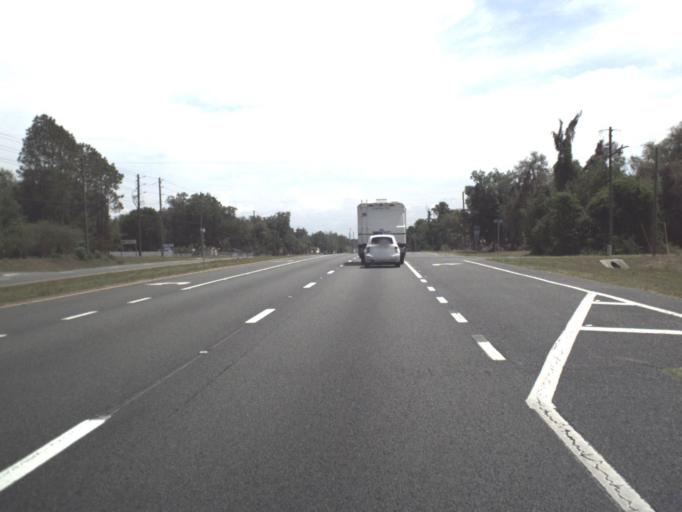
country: US
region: Florida
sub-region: Sumter County
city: Wildwood
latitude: 28.8321
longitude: -81.9998
